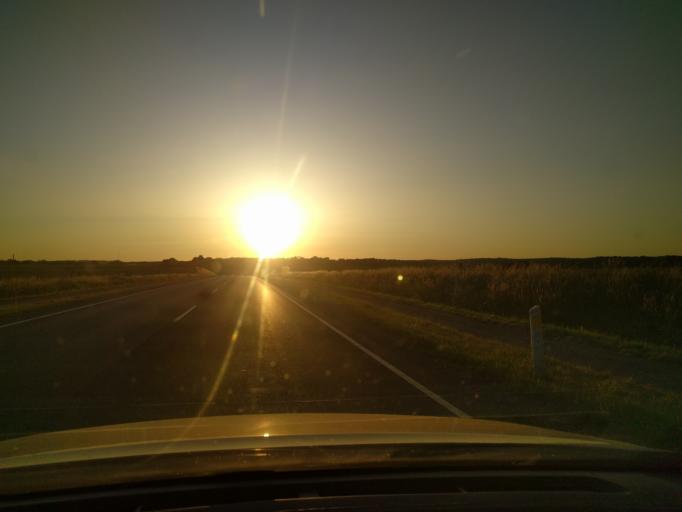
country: DK
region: Zealand
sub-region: Slagelse Kommune
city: Slagelse
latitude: 55.3644
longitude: 11.4286
